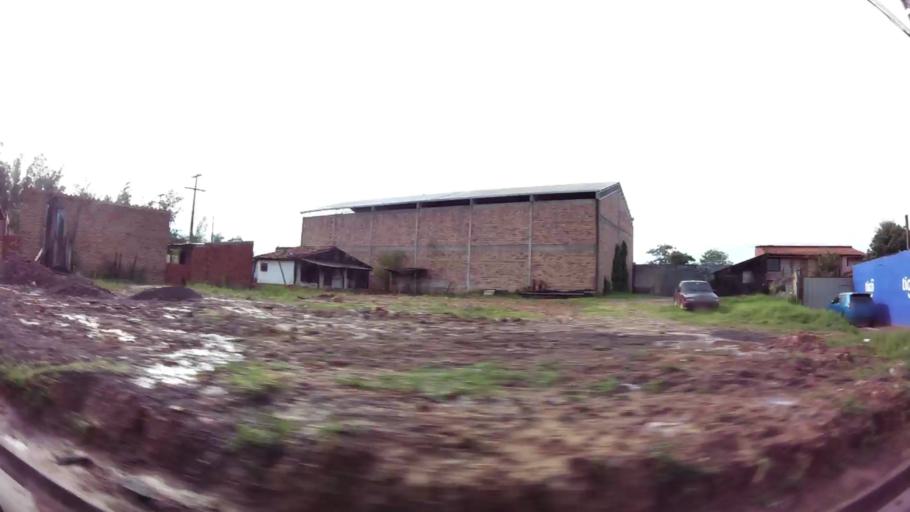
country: PY
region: Central
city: Limpio
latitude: -25.1879
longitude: -57.4965
